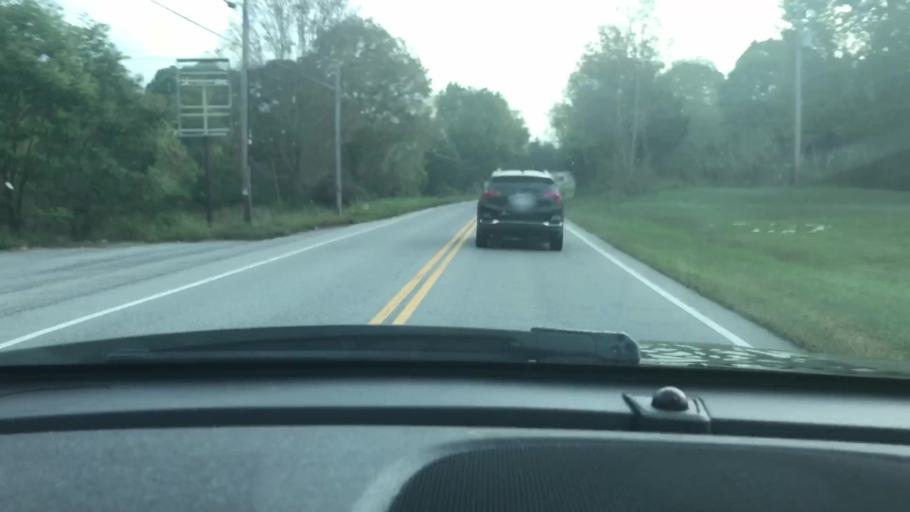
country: US
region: Tennessee
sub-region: Dickson County
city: Charlotte
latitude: 36.2568
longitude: -87.2271
